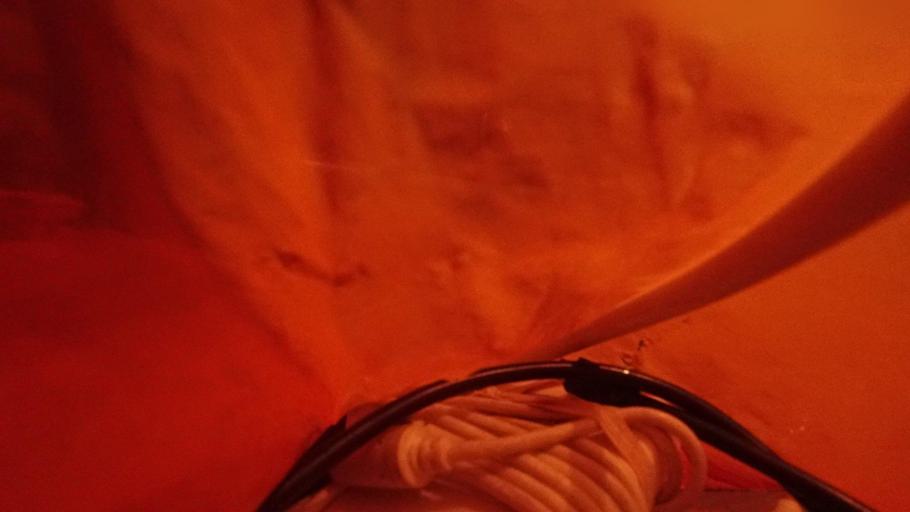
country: RU
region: Jewish Autonomous Oblast
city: Khingansk
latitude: 49.1635
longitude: 130.7654
